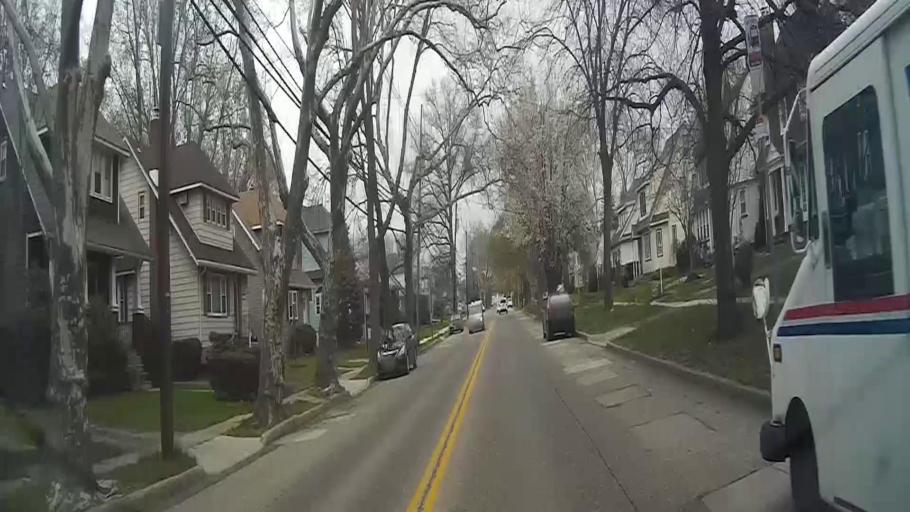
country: US
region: New Jersey
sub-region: Camden County
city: Haddon Heights
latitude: 39.8832
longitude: -75.0694
